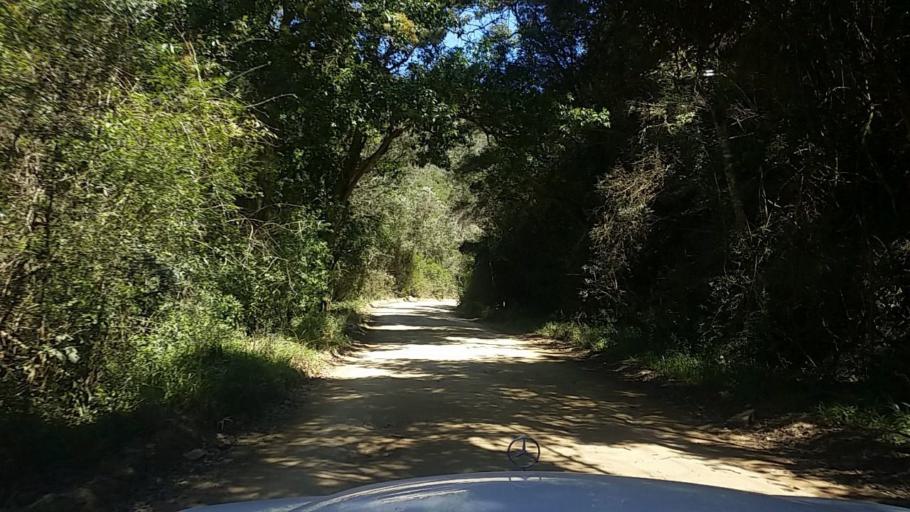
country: ZA
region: Western Cape
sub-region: Eden District Municipality
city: Knysna
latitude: -33.8604
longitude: 23.1746
